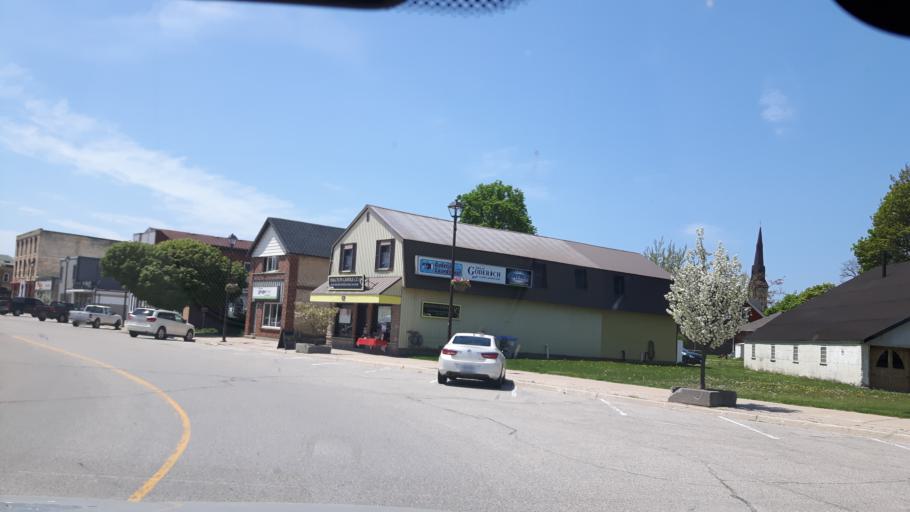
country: CA
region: Ontario
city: Goderich
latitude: 43.7452
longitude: -81.7083
